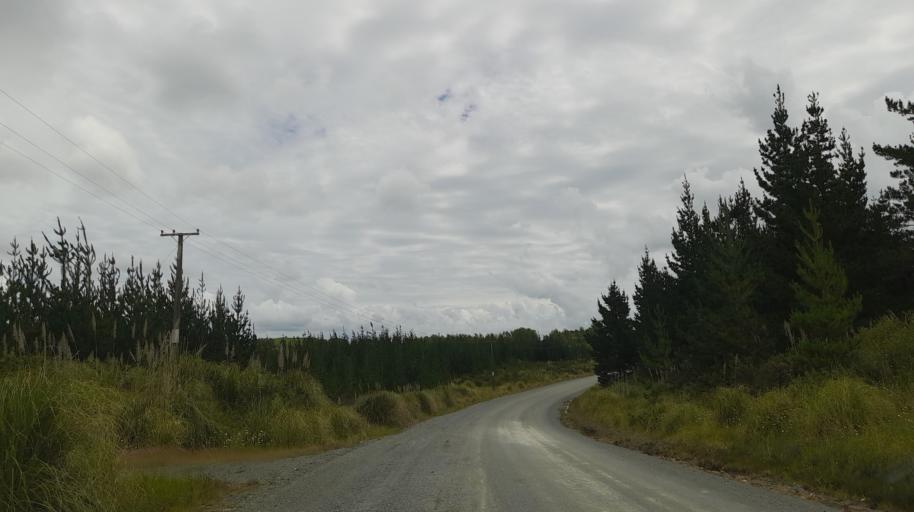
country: NZ
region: Auckland
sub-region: Auckland
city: Wellsford
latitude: -36.2318
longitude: 174.4429
